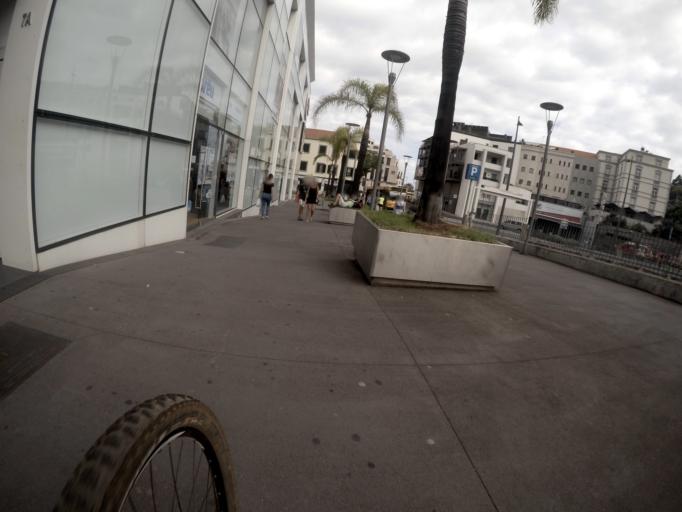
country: PT
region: Madeira
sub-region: Funchal
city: Funchal
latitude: 32.6474
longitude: -16.9141
